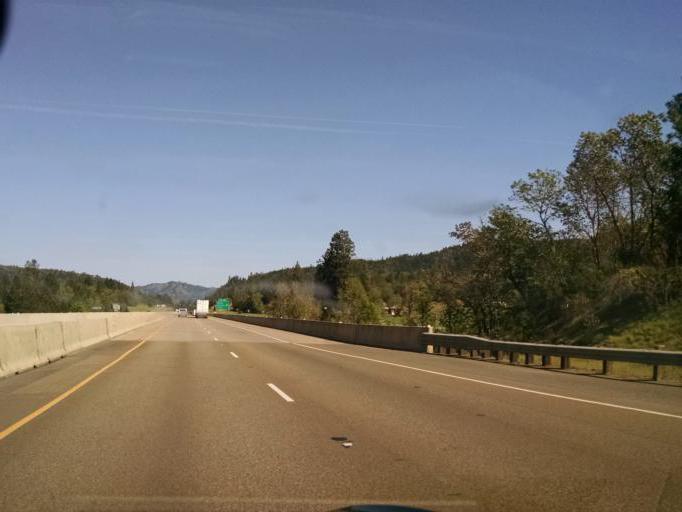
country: US
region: Oregon
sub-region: Douglas County
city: Riddle
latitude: 42.9478
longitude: -123.3252
